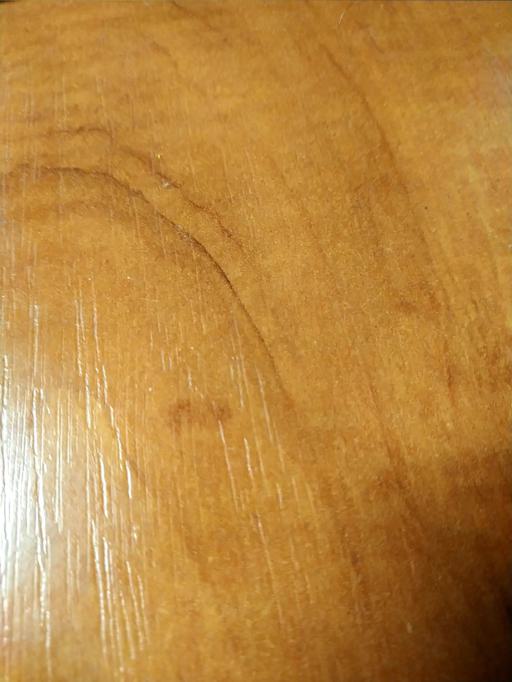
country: RU
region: Smolensk
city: Yartsevo
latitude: 55.4284
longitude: 32.8268
